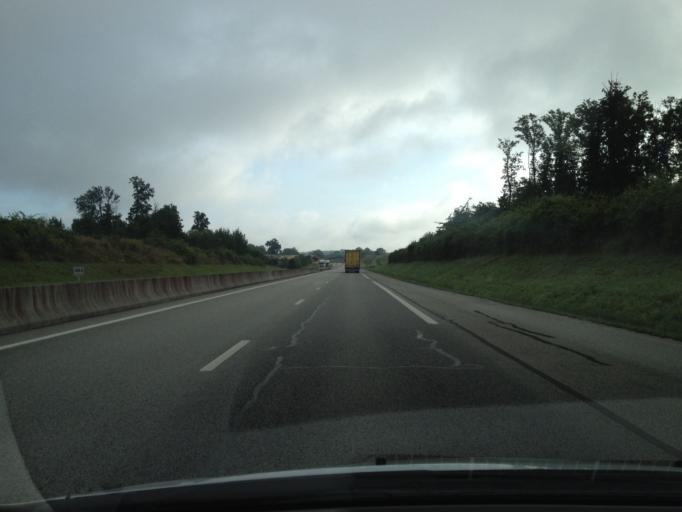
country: FR
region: Lower Normandy
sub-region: Departement de l'Orne
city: Radon
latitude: 48.5218
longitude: 0.1489
